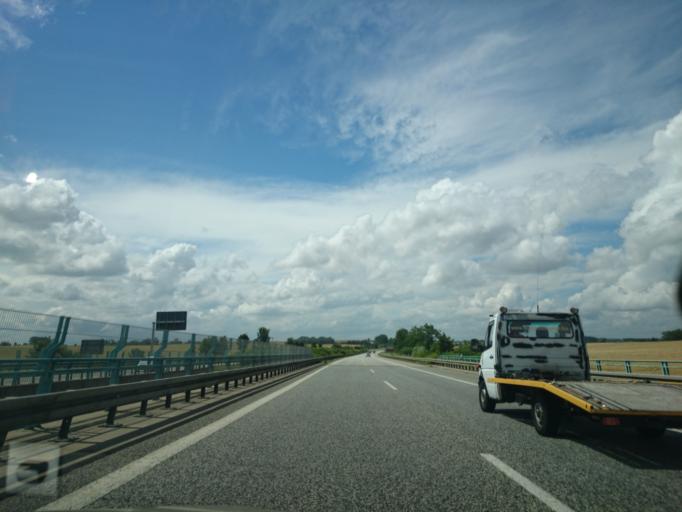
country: DE
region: Mecklenburg-Vorpommern
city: Lubow
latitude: 53.8625
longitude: 11.5041
